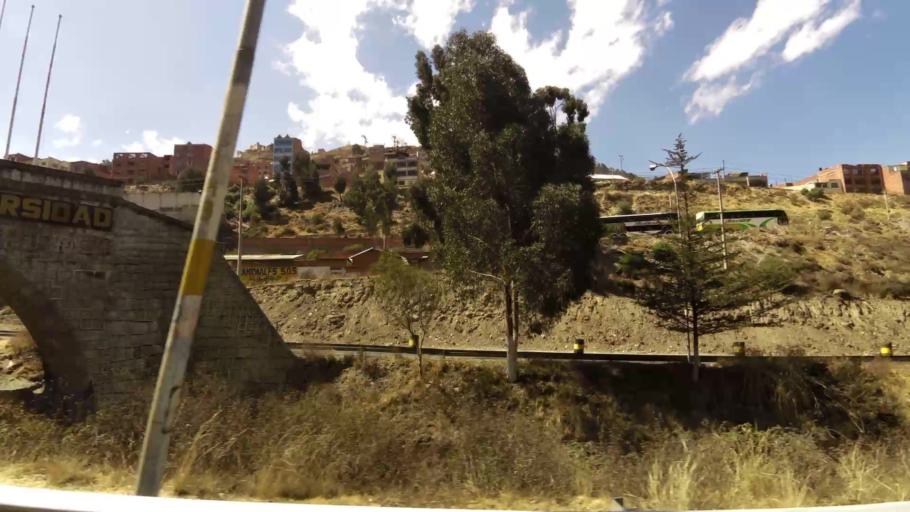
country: BO
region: La Paz
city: La Paz
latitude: -16.4713
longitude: -68.1524
